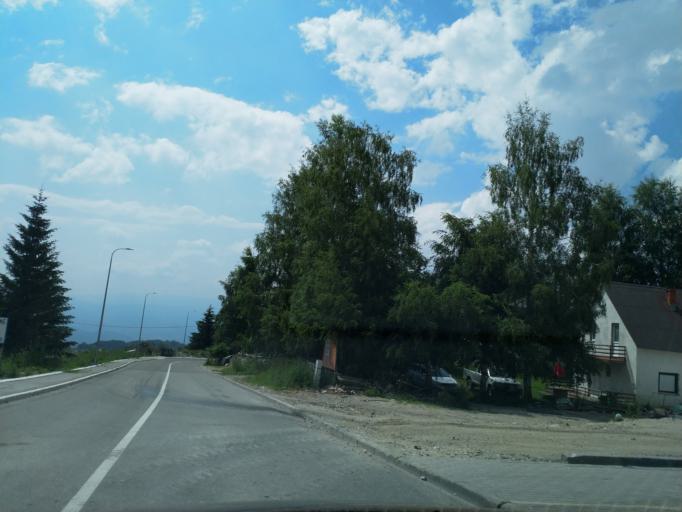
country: RS
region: Central Serbia
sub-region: Raski Okrug
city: Raska
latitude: 43.2750
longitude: 20.7658
